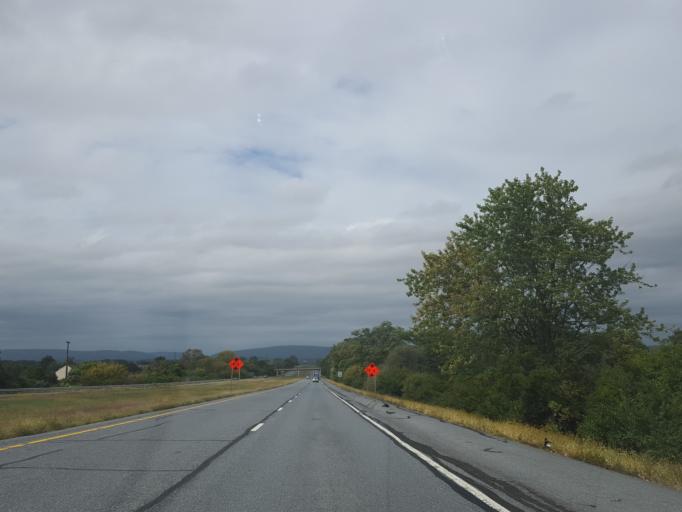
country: US
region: Maryland
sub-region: Frederick County
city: Jefferson
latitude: 39.3587
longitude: -77.5412
